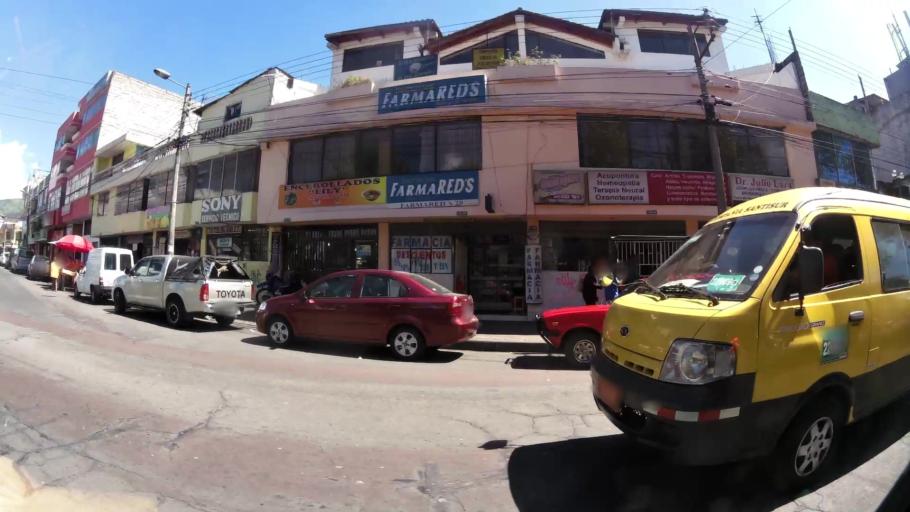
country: EC
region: Pichincha
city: Quito
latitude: -0.2621
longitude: -78.5374
